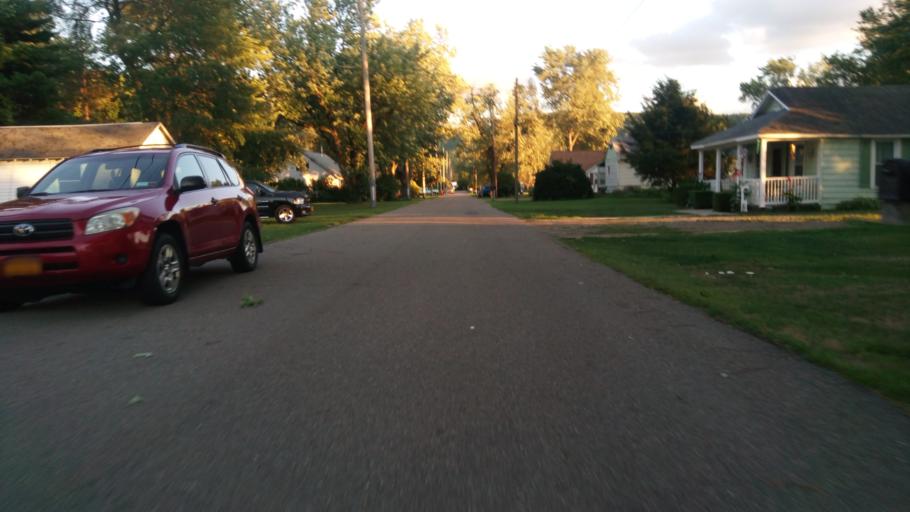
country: US
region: New York
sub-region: Chemung County
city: Southport
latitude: 42.0626
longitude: -76.7926
